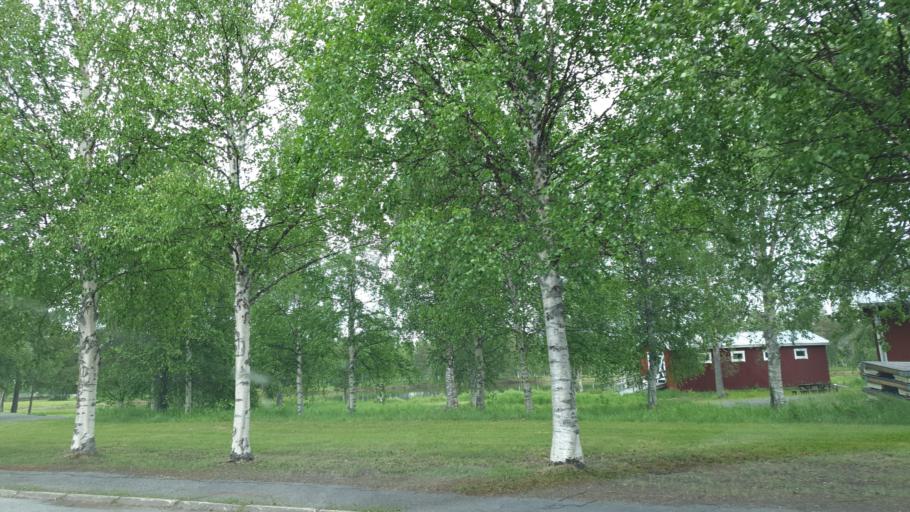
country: SE
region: Vaesterbotten
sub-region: Sorsele Kommun
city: Sorsele
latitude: 65.5343
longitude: 17.5274
